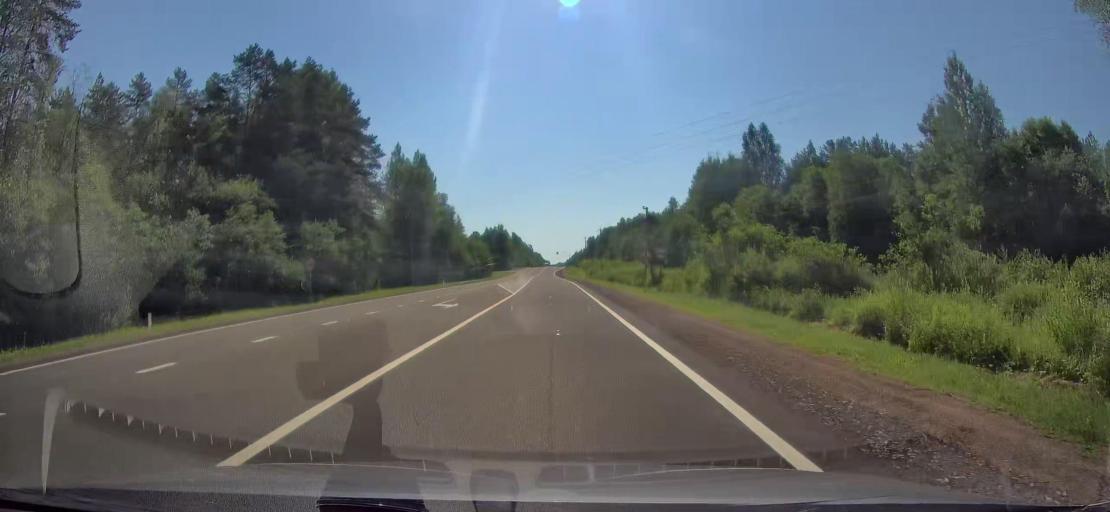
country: RU
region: Leningrad
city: Yefimovskiy
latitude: 59.3985
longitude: 34.7344
